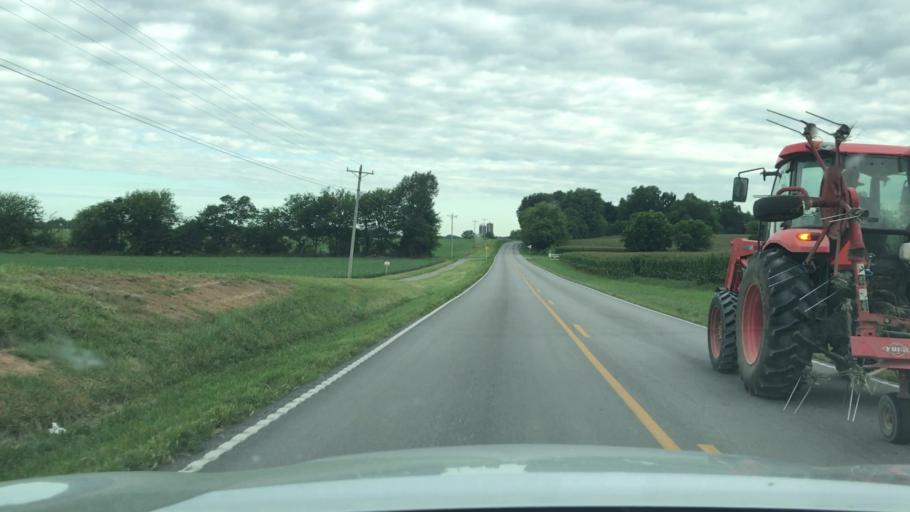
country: US
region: Kentucky
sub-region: Todd County
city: Guthrie
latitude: 36.6882
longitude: -87.2011
